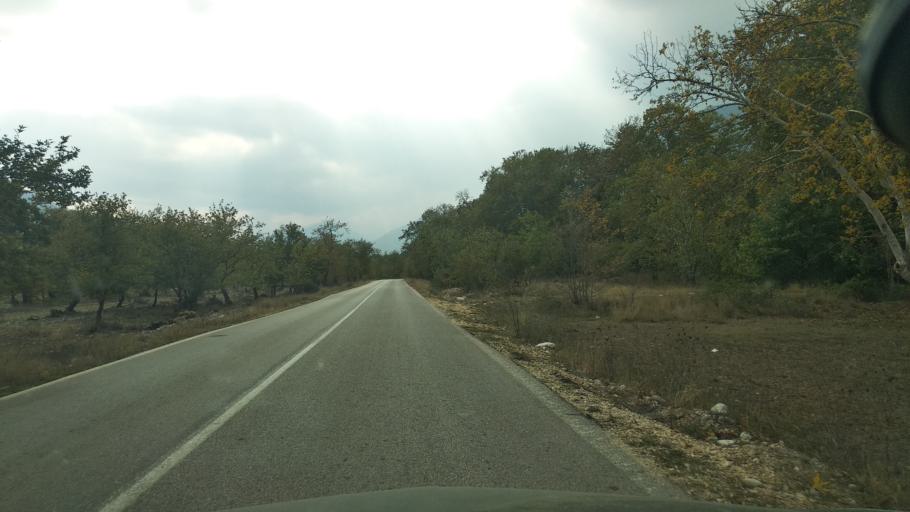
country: GR
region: Thessaly
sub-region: Trikala
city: Kastraki
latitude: 39.7000
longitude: 21.5251
